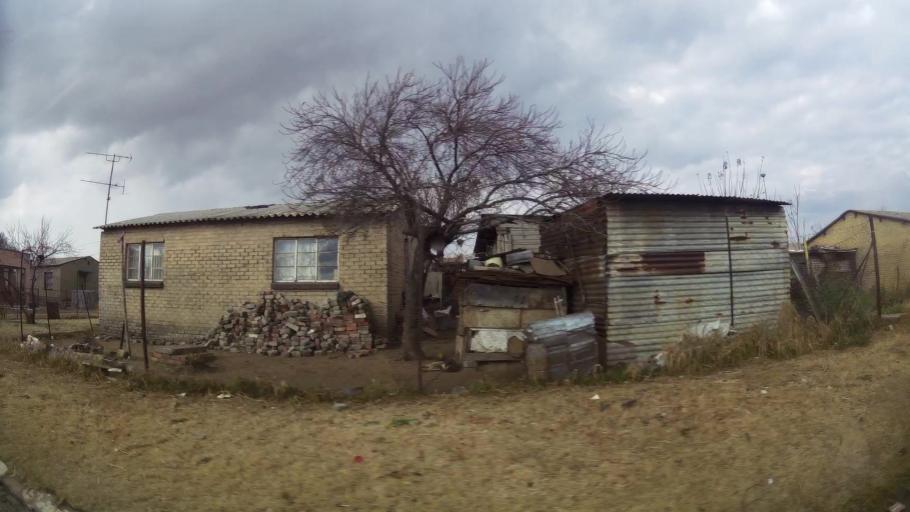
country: ZA
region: Orange Free State
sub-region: Fezile Dabi District Municipality
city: Sasolburg
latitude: -26.8413
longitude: 27.8437
